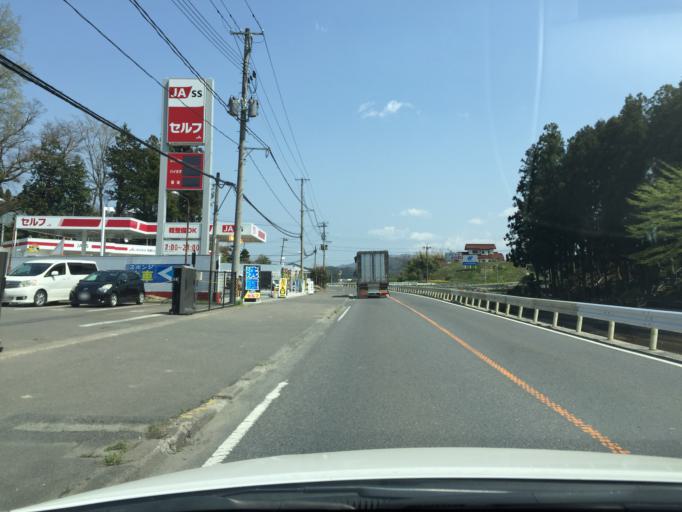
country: JP
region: Fukushima
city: Funehikimachi-funehiki
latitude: 37.4414
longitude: 140.6269
